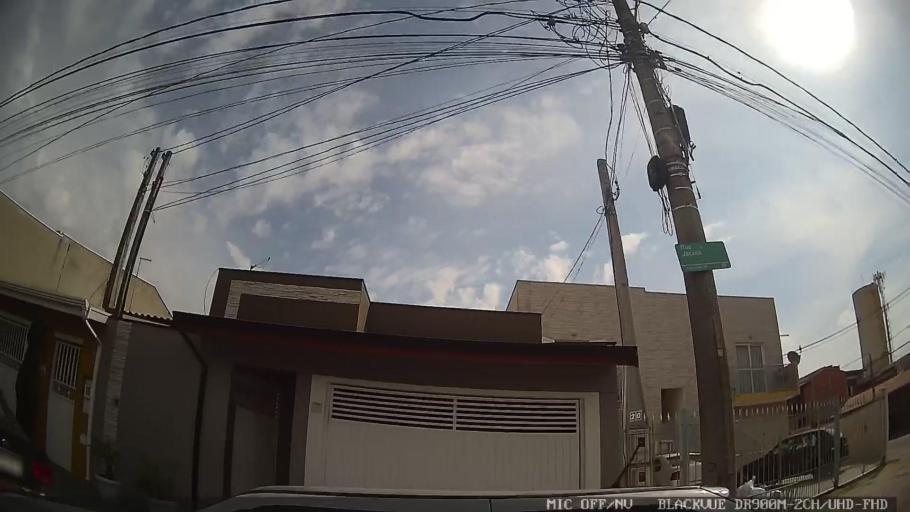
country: BR
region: Sao Paulo
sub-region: Indaiatuba
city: Indaiatuba
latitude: -23.1220
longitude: -47.2514
